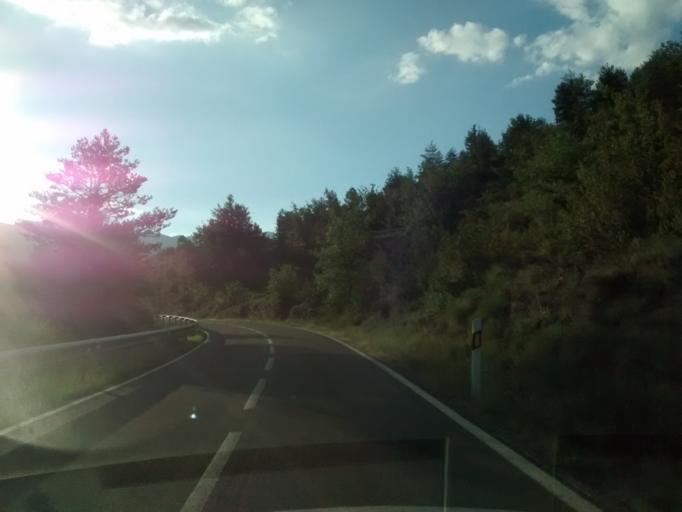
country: ES
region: Aragon
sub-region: Provincia de Huesca
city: Boltana
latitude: 42.4725
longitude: -0.0025
